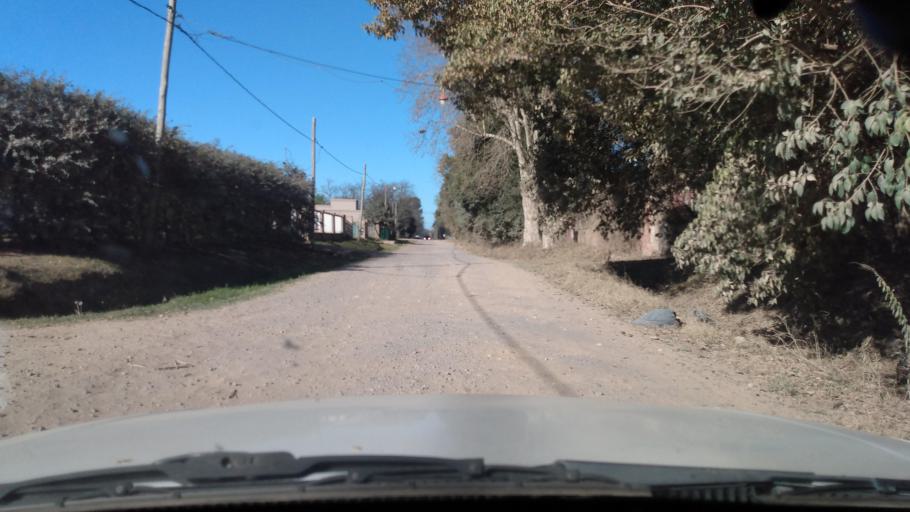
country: AR
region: Buenos Aires
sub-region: Partido de Mercedes
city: Mercedes
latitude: -34.6491
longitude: -59.4071
